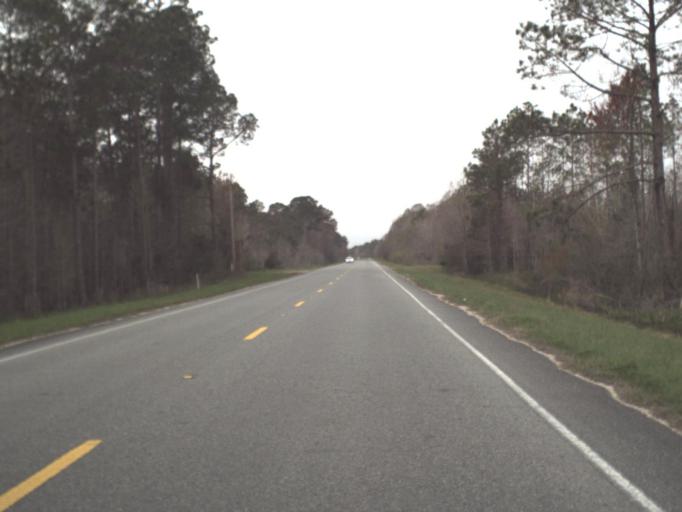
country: US
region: Florida
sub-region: Leon County
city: Woodville
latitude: 30.1915
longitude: -84.0837
